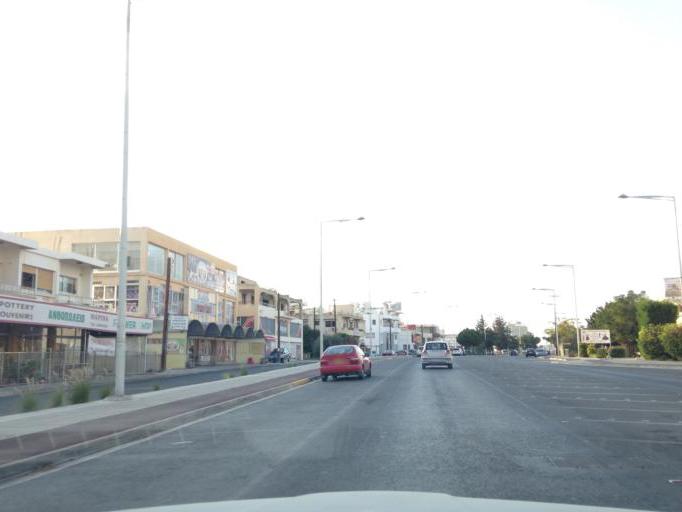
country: CY
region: Pafos
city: Paphos
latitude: 34.7641
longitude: 32.4477
